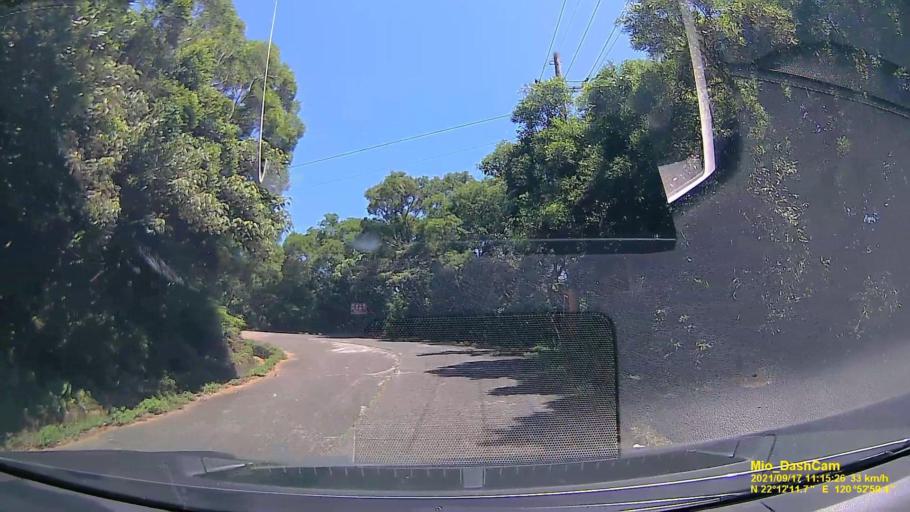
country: TW
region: Taiwan
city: Hengchun
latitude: 22.2032
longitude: 120.8832
